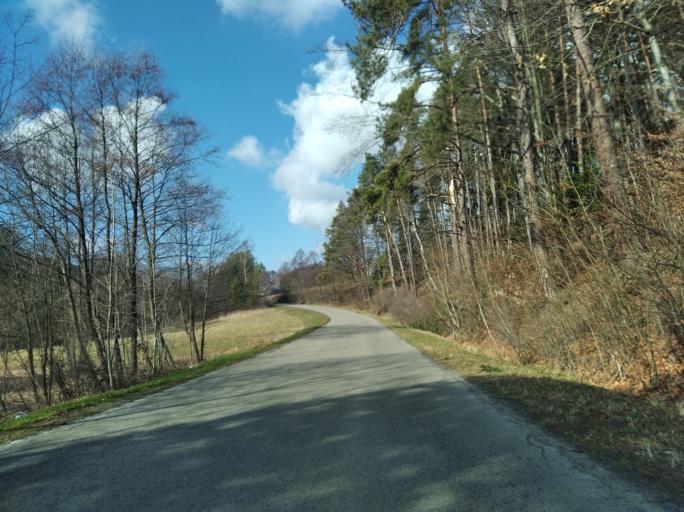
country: PL
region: Subcarpathian Voivodeship
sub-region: Powiat strzyzowski
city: Frysztak
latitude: 49.8660
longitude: 21.5429
